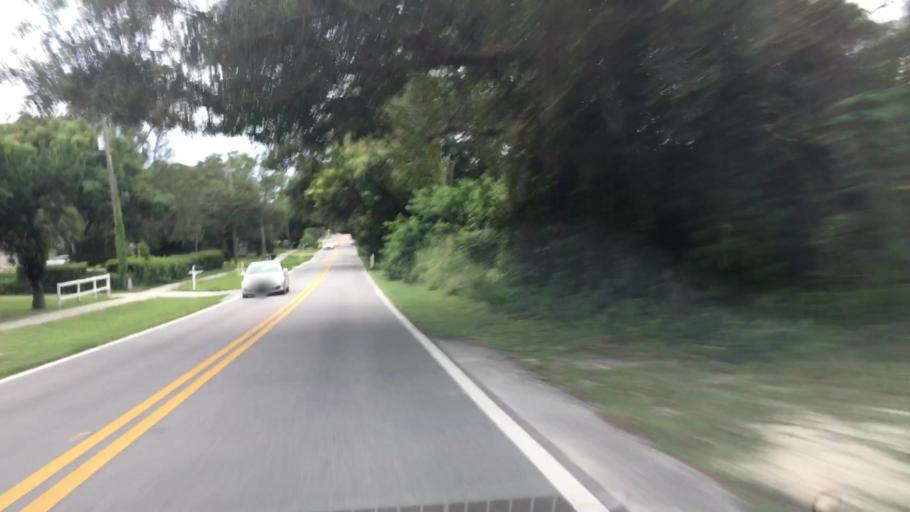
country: US
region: Florida
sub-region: Volusia County
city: DeBary
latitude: 28.8903
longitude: -81.3009
